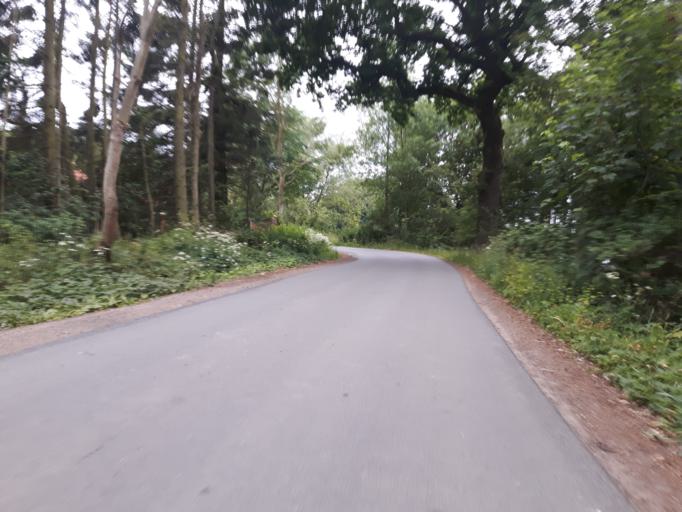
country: DE
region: Schleswig-Holstein
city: Schashagen
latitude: 54.1156
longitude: 10.9031
